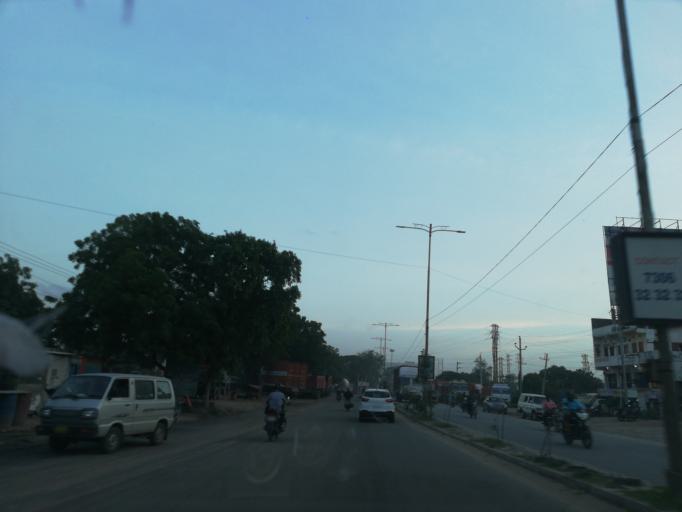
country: IN
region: Telangana
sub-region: Medak
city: Serilingampalle
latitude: 17.5358
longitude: 78.3581
